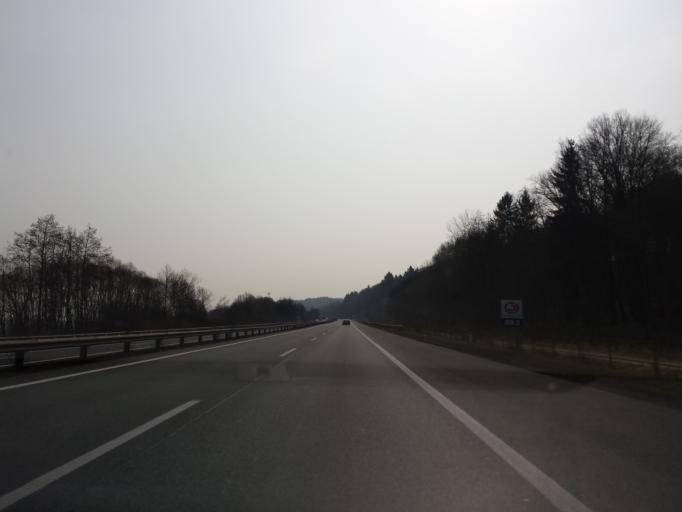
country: AT
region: Styria
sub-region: Politischer Bezirk Weiz
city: Sinabelkirchen
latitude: 47.0949
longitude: 15.8274
